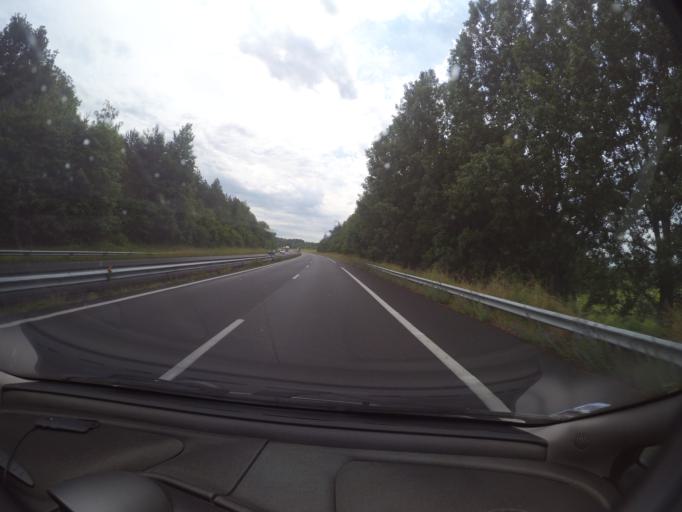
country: FR
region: Pays de la Loire
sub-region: Departement de Maine-et-Loire
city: Seiches-sur-le-Loir
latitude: 47.5778
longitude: -0.3349
